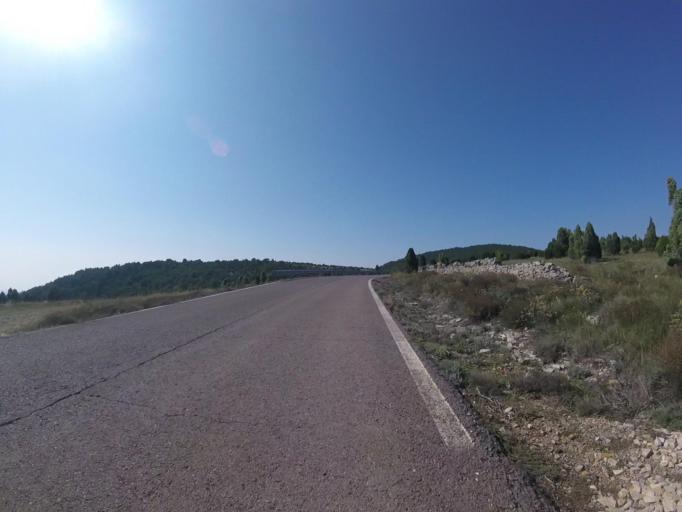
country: ES
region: Valencia
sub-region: Provincia de Castello
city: Benafigos
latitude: 40.2805
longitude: -0.2392
